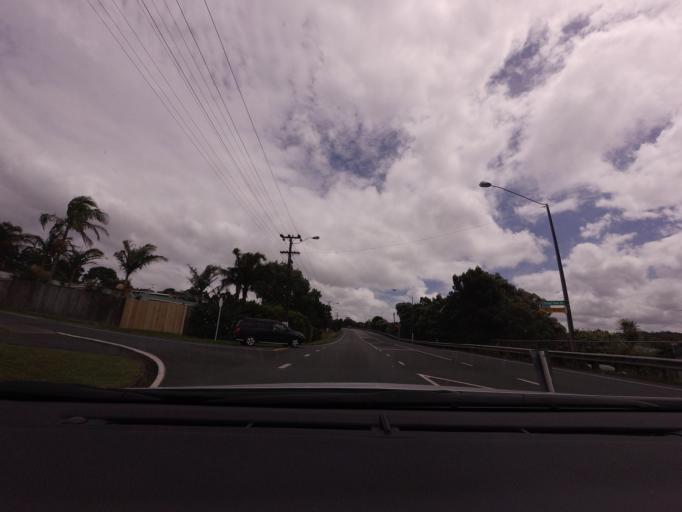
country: NZ
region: Auckland
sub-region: Auckland
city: Rothesay Bay
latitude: -36.5668
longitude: 174.6931
